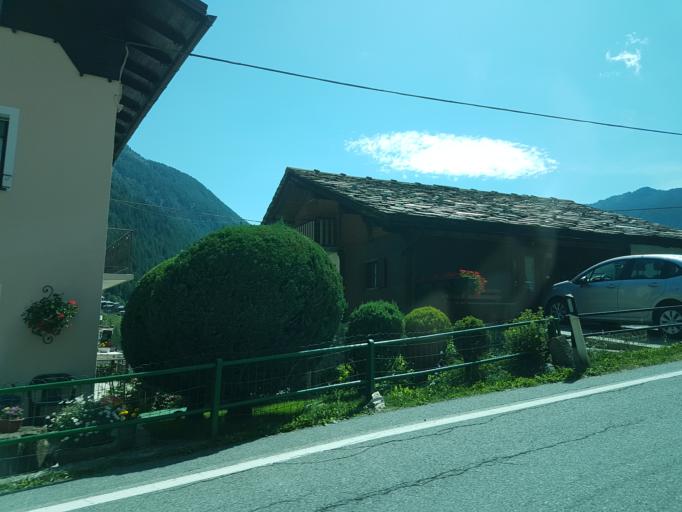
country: IT
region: Aosta Valley
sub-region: Valle d'Aosta
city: Valtournenche
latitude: 45.8728
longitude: 7.6225
